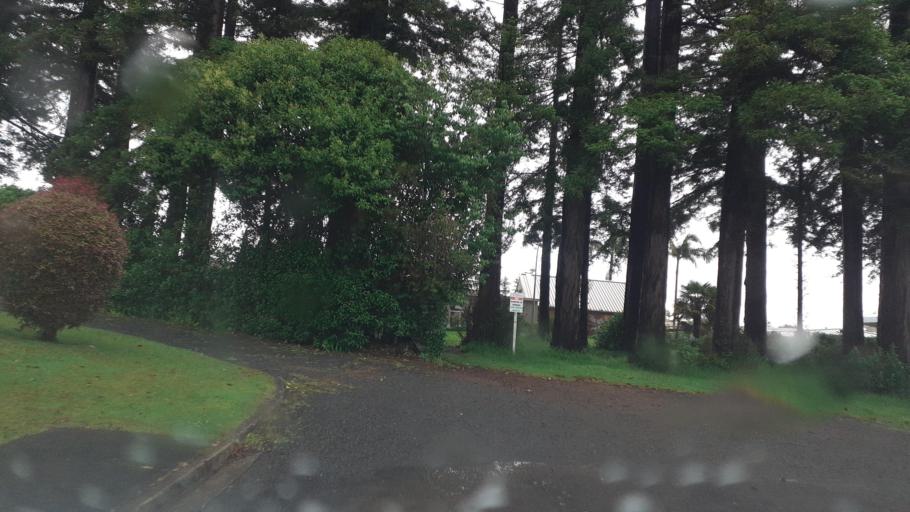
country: NZ
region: Northland
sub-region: Far North District
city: Kerikeri
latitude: -35.2242
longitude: 173.9542
